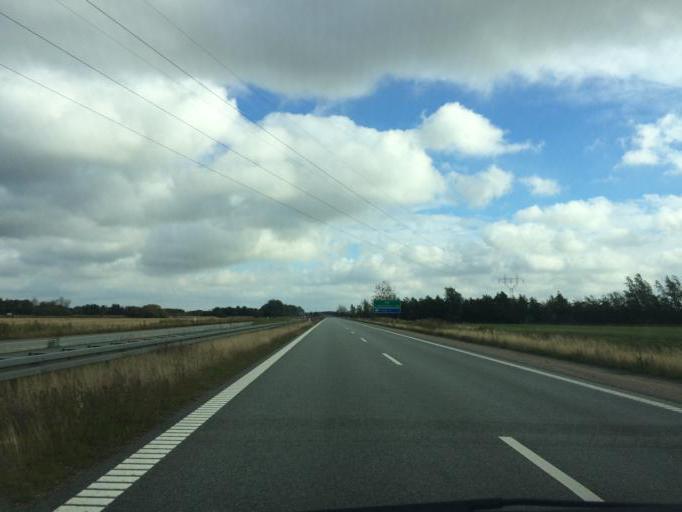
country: DK
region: North Denmark
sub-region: Alborg Kommune
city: Vodskov
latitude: 57.0992
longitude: 10.0274
